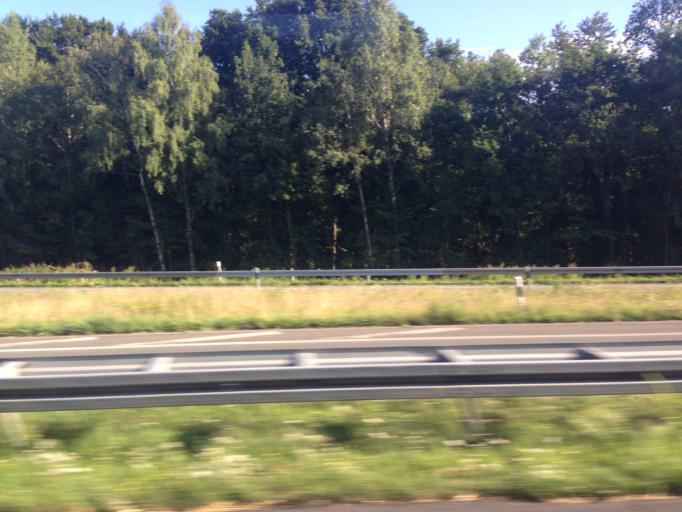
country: DE
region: North Rhine-Westphalia
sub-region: Regierungsbezirk Munster
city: Muenster
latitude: 51.9158
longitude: 7.5652
